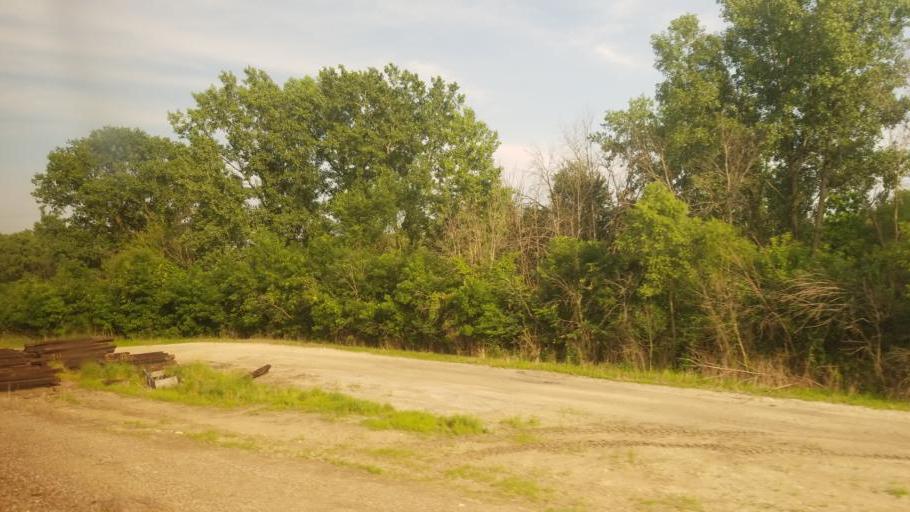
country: US
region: Illinois
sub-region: DuPage County
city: Warrenville
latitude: 41.7758
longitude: -88.2369
